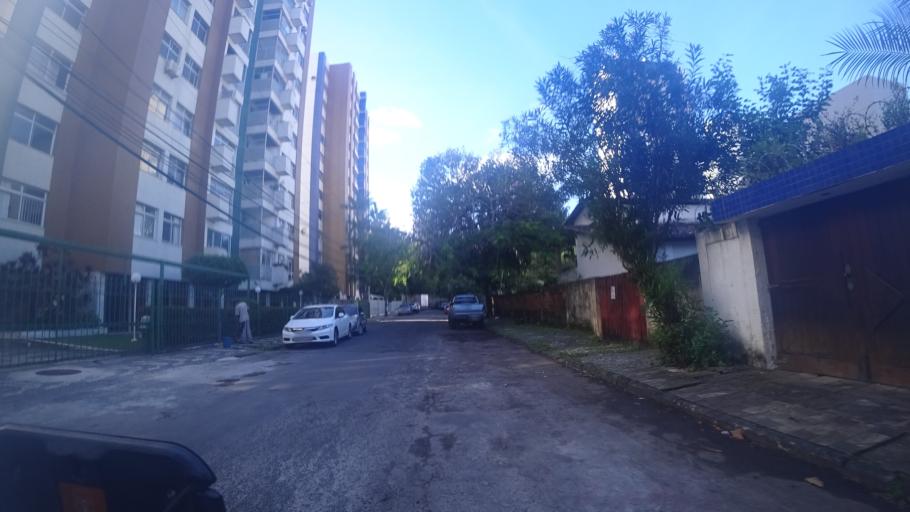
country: BR
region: Bahia
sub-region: Salvador
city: Salvador
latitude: -12.9928
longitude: -38.4563
